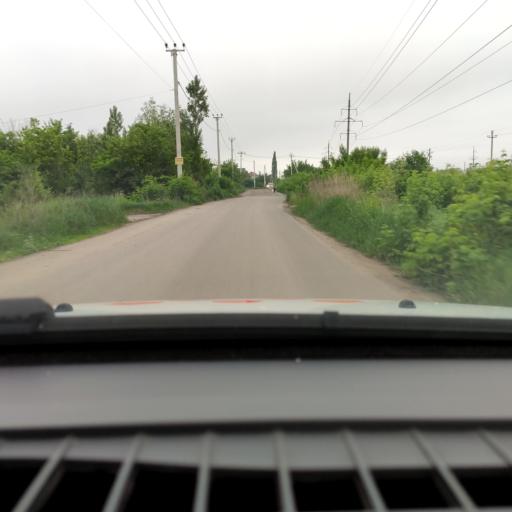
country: RU
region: Voronezj
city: Novaya Usman'
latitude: 51.6596
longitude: 39.4089
